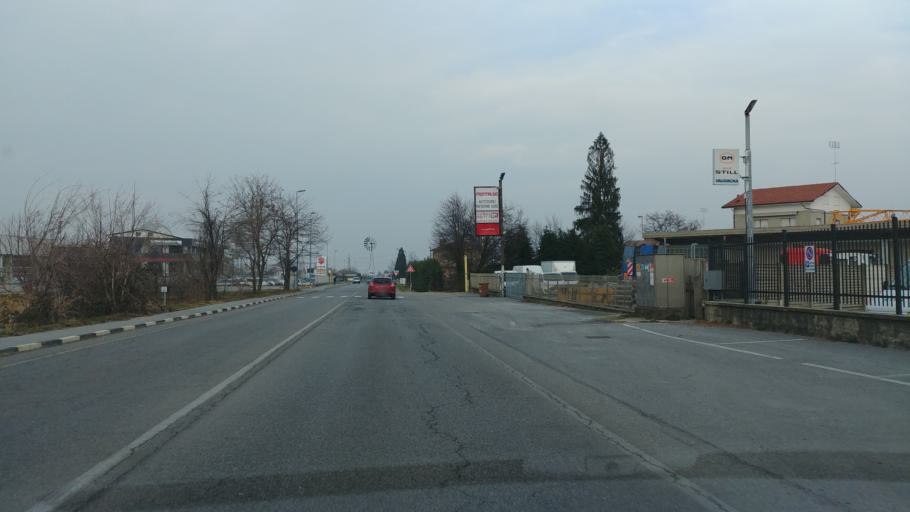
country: IT
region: Piedmont
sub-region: Provincia di Cuneo
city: Borgo San Dalmazzo
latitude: 44.3518
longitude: 7.5091
